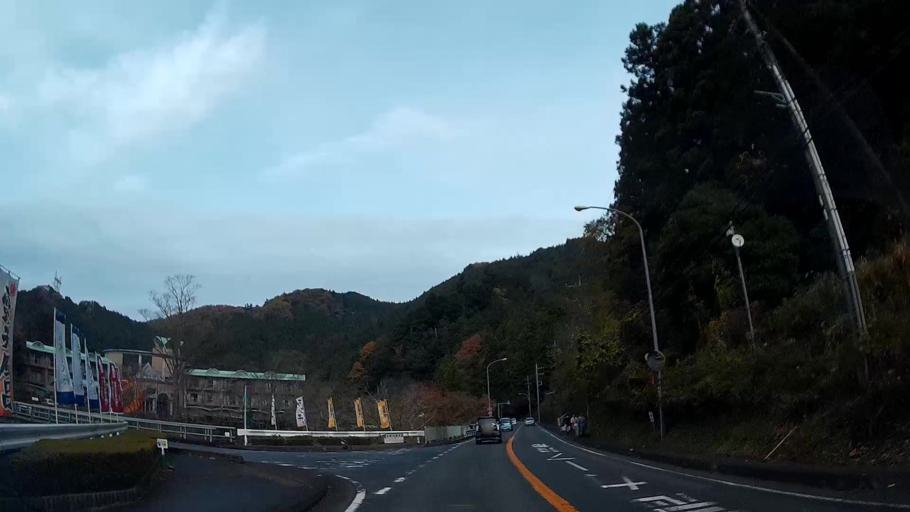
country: JP
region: Saitama
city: Morohongo
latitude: 35.9203
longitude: 139.2111
